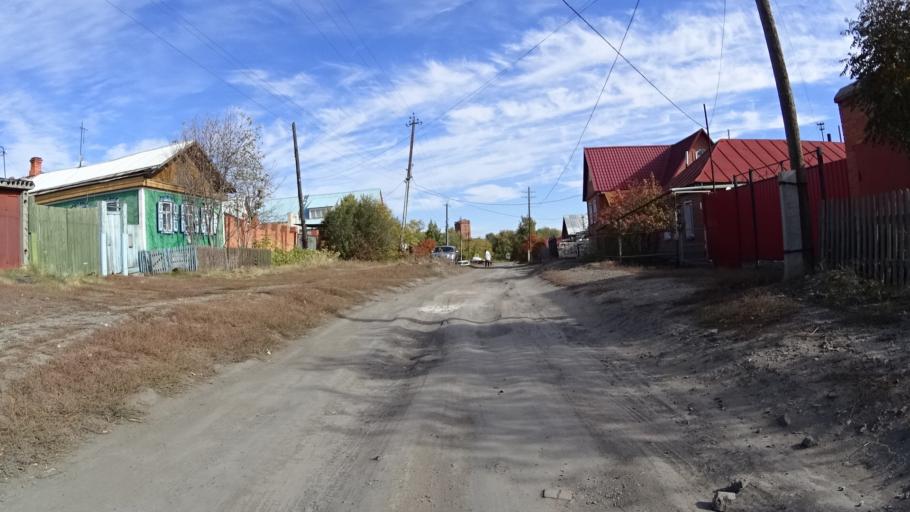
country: RU
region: Chelyabinsk
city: Troitsk
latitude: 54.0760
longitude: 61.5850
